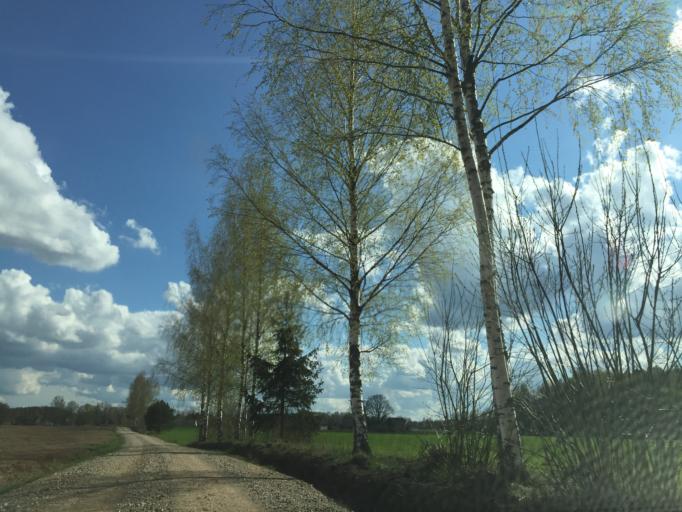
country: LV
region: Beverina
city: Murmuiza
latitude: 57.4242
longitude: 25.5495
